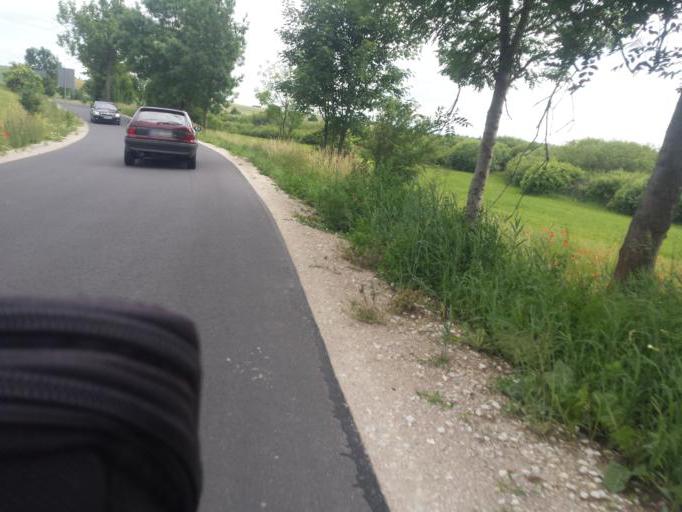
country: PL
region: Warmian-Masurian Voivodeship
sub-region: Powiat ilawski
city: Ilawa
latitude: 53.5176
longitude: 19.5545
